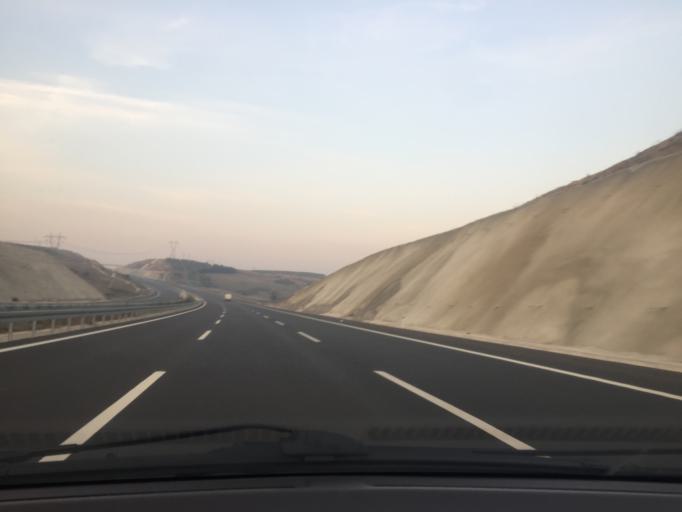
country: TR
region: Bursa
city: Mahmudiye
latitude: 40.2764
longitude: 28.5167
